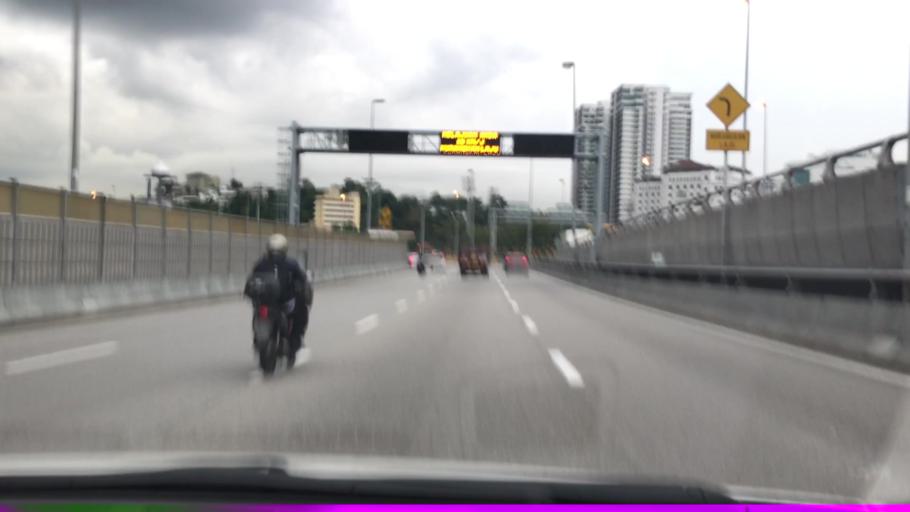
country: MY
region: Kuala Lumpur
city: Kuala Lumpur
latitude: 3.1173
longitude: 101.6628
